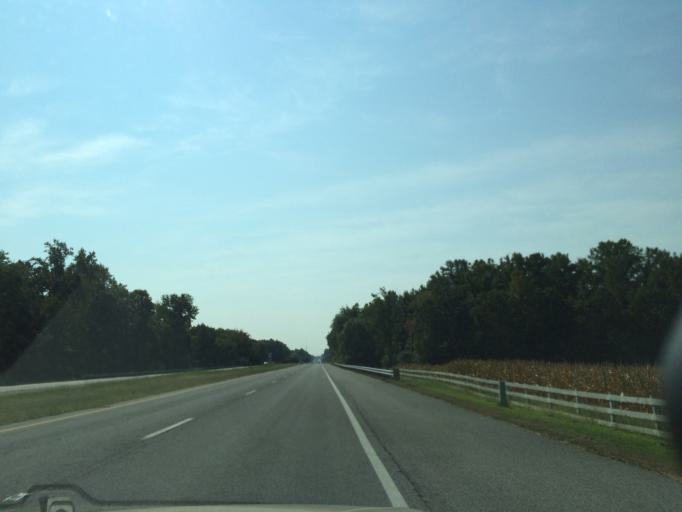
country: US
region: Maryland
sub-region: Charles County
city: La Plata
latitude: 38.4427
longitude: -76.9837
